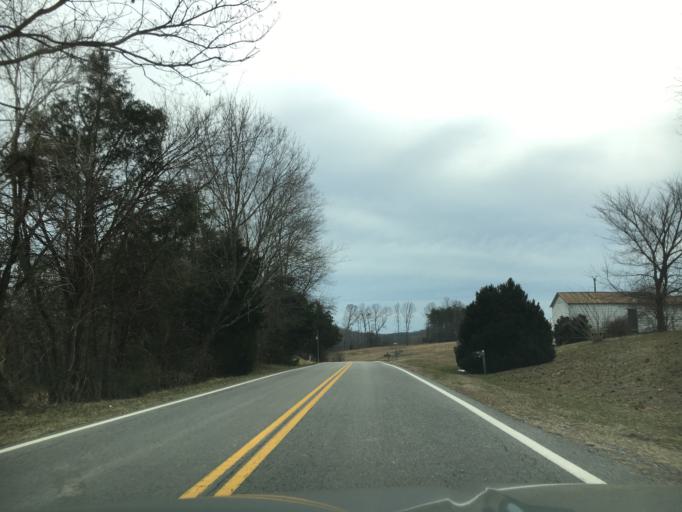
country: US
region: Virginia
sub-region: Charlotte County
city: Charlotte Court House
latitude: 37.1212
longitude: -78.7577
